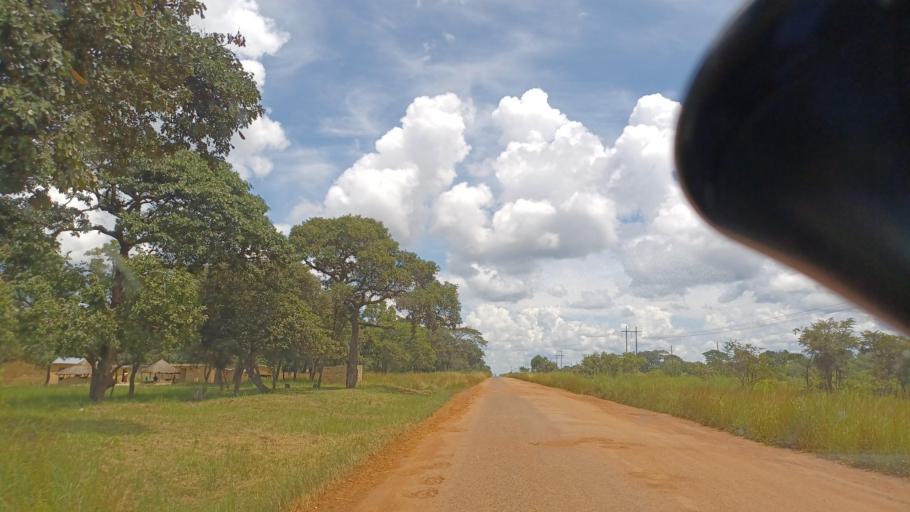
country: ZM
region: North-Western
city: Solwezi
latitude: -12.4915
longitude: 26.1894
